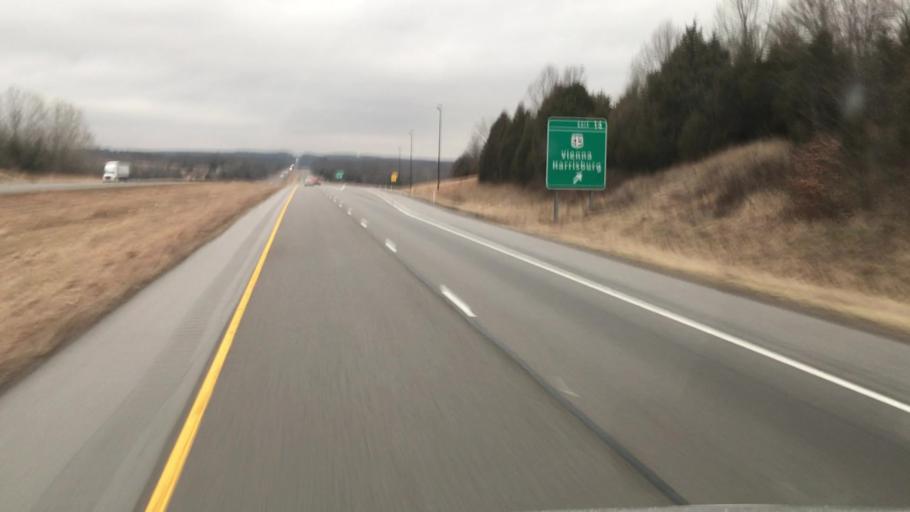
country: US
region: Illinois
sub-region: Johnson County
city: Vienna
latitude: 37.4410
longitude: -88.8857
